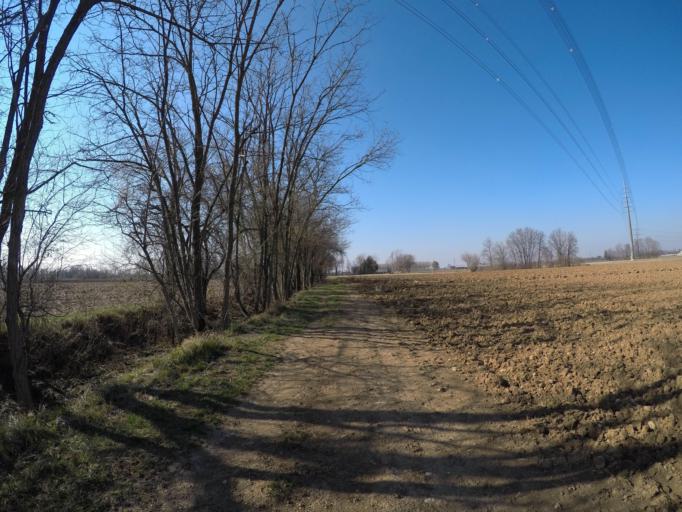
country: IT
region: Friuli Venezia Giulia
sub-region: Provincia di Udine
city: Lestizza
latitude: 45.9833
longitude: 13.1606
